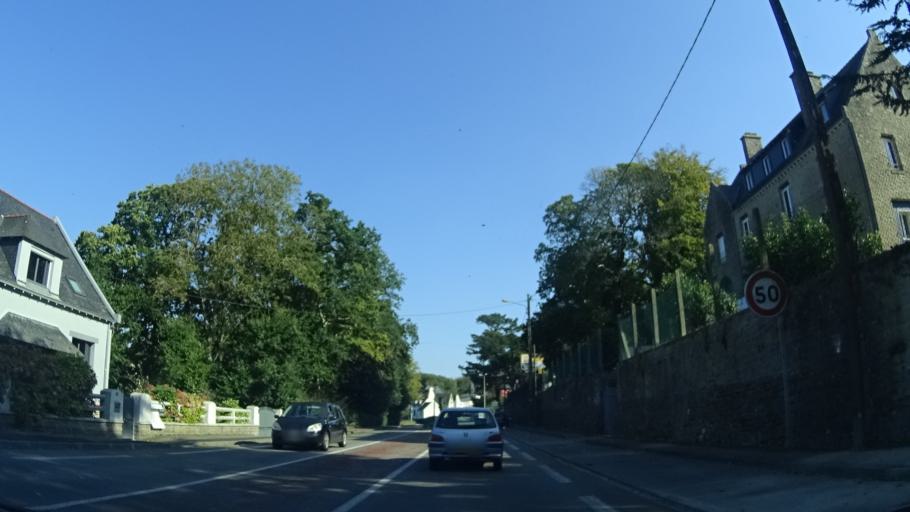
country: FR
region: Brittany
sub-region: Departement du Finistere
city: Douarnenez
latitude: 48.0882
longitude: -4.3077
